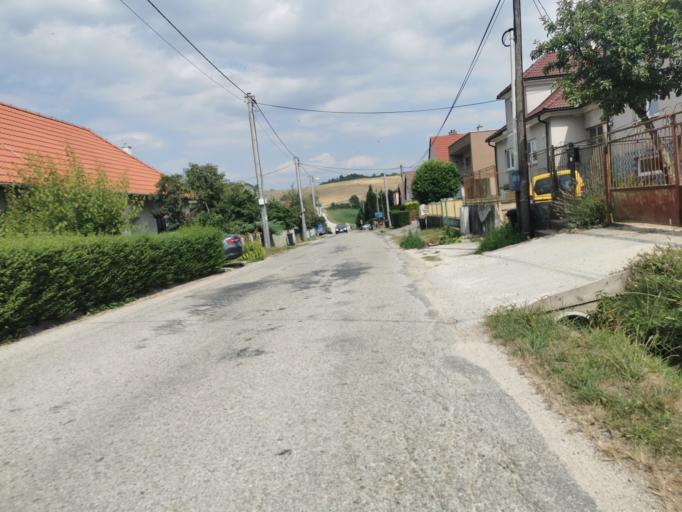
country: SK
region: Trenciansky
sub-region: Okres Myjava
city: Myjava
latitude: 48.7224
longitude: 17.5203
